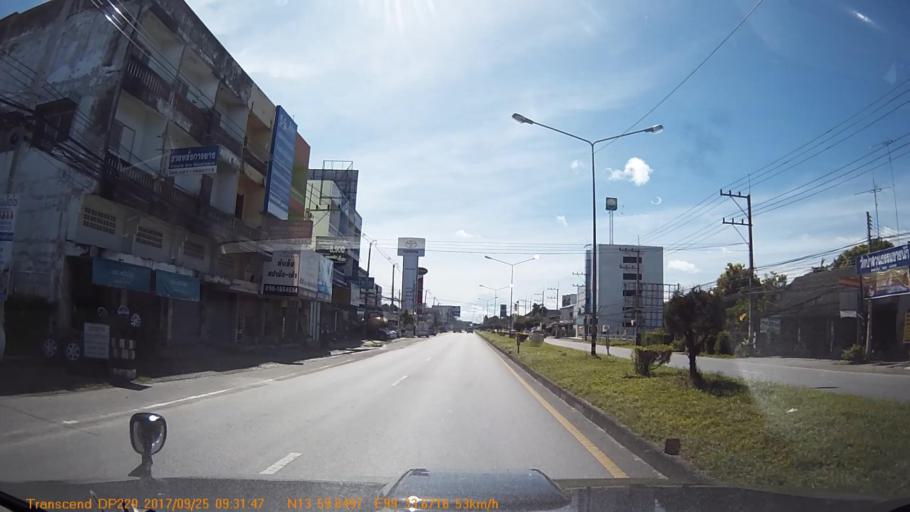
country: TH
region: Kanchanaburi
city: Kanchanaburi
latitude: 13.9940
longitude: 99.5614
